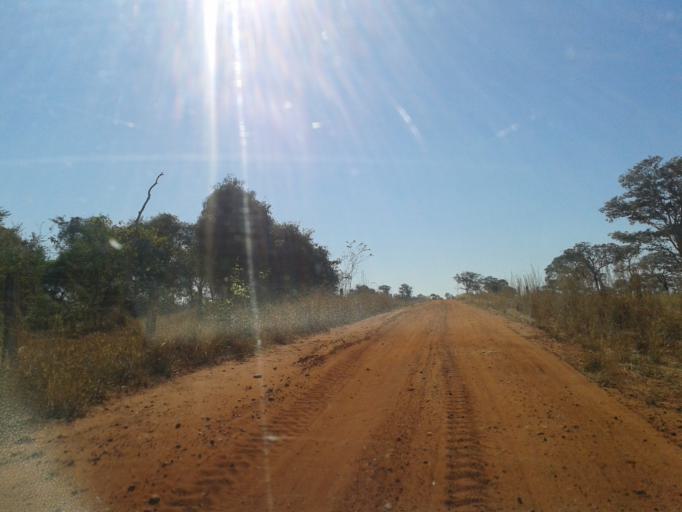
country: BR
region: Minas Gerais
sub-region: Santa Vitoria
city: Santa Vitoria
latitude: -19.0335
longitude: -50.3650
